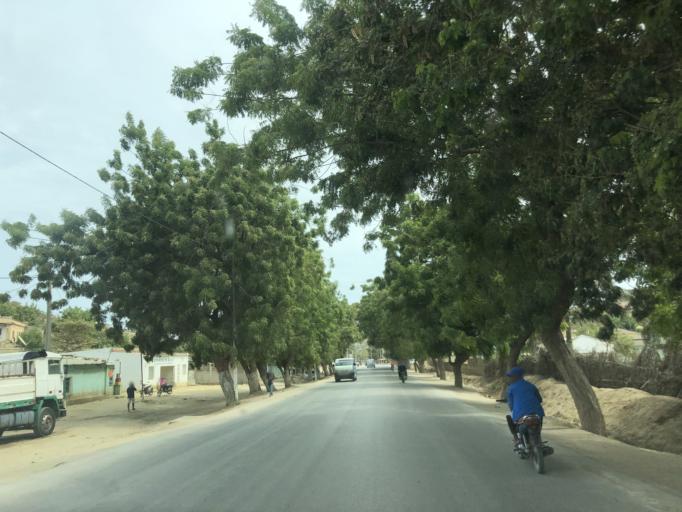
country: AO
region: Cuanza Sul
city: Sumbe
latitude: -11.2179
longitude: 13.8475
